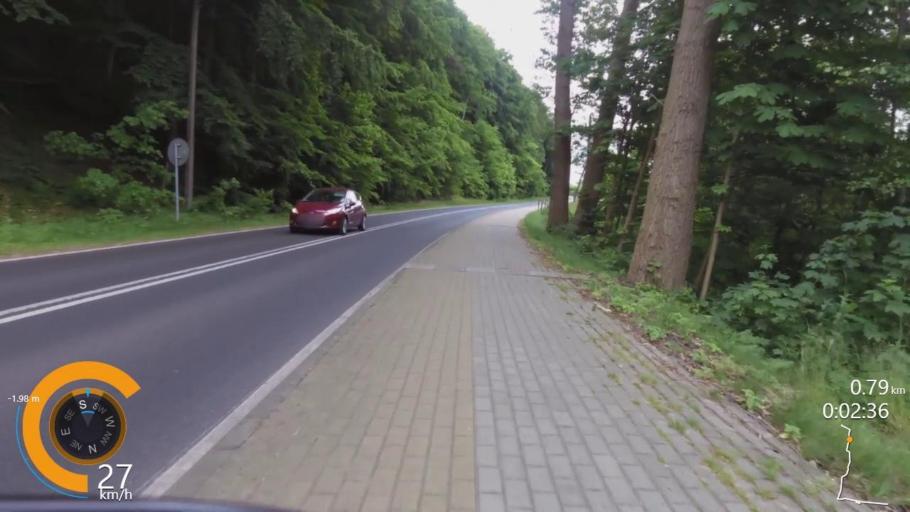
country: PL
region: West Pomeranian Voivodeship
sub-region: Powiat kamienski
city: Miedzyzdroje
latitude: 53.9063
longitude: 14.4377
